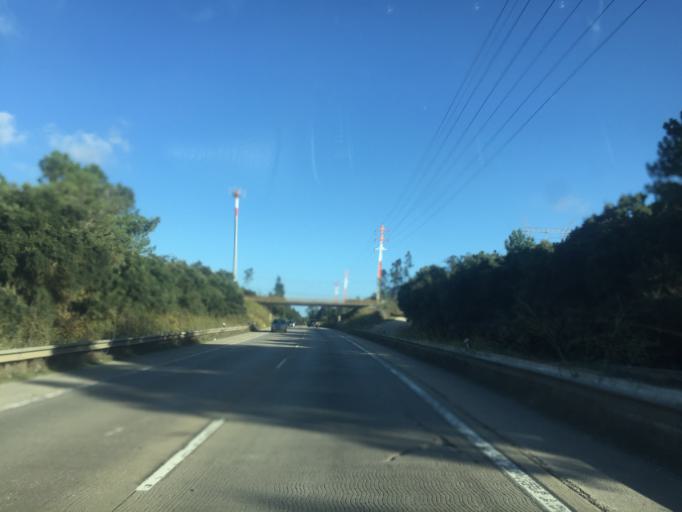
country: PT
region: Santarem
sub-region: Rio Maior
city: Rio Maior
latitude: 39.3610
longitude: -8.9685
